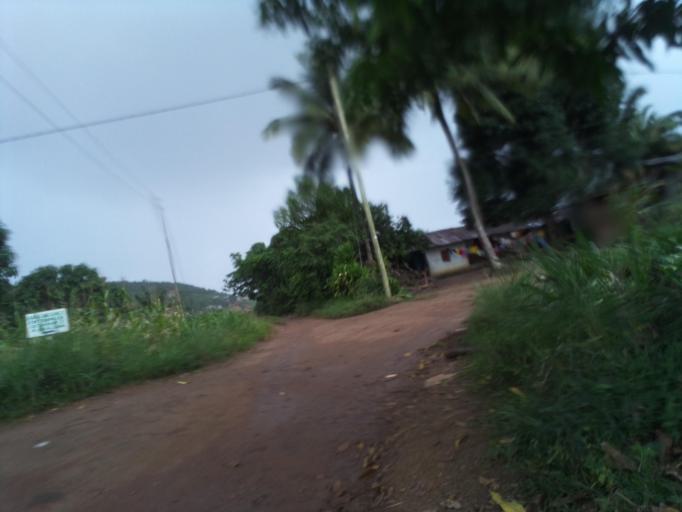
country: SL
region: Eastern Province
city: Kenema
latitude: 7.8554
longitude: -11.1943
